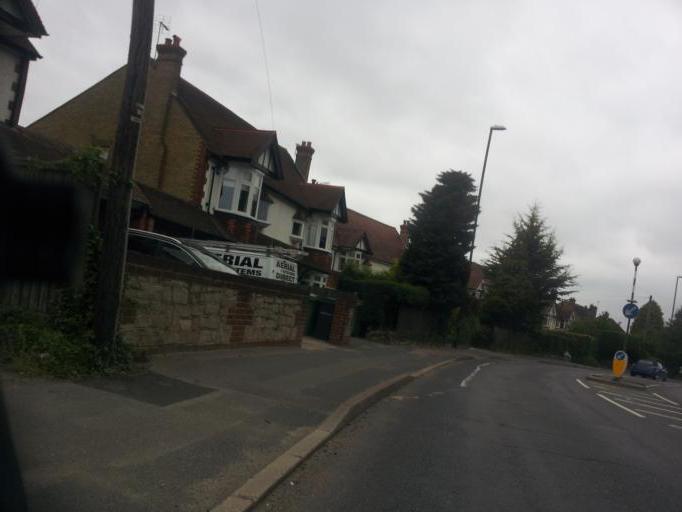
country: GB
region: England
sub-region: Kent
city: Maidstone
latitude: 51.2532
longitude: 0.5274
